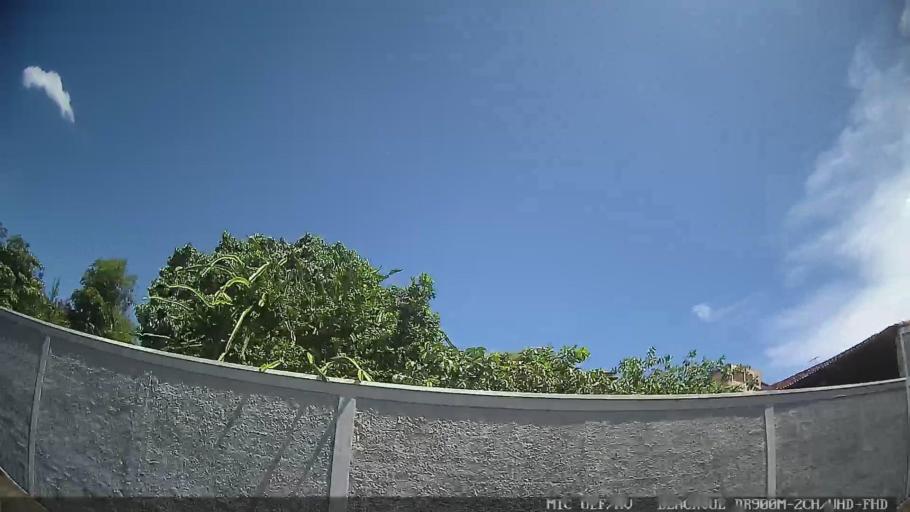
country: BR
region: Sao Paulo
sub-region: Pedreira
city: Pedreira
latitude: -22.7483
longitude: -46.9138
